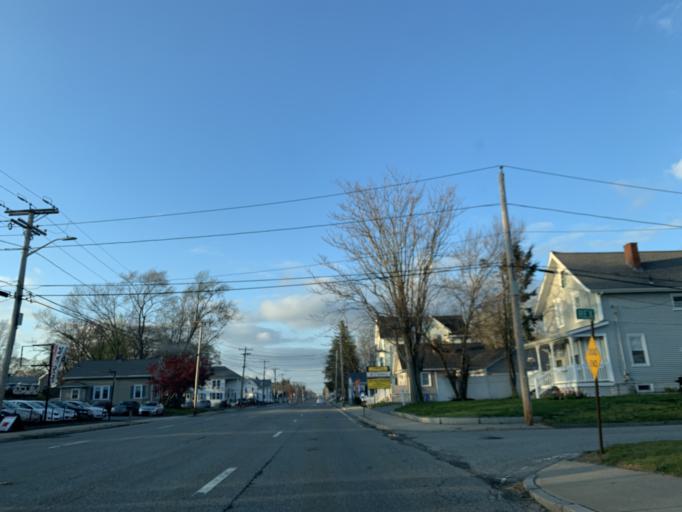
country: US
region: Rhode Island
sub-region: Providence County
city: Valley Falls
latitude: 41.9021
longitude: -71.3673
